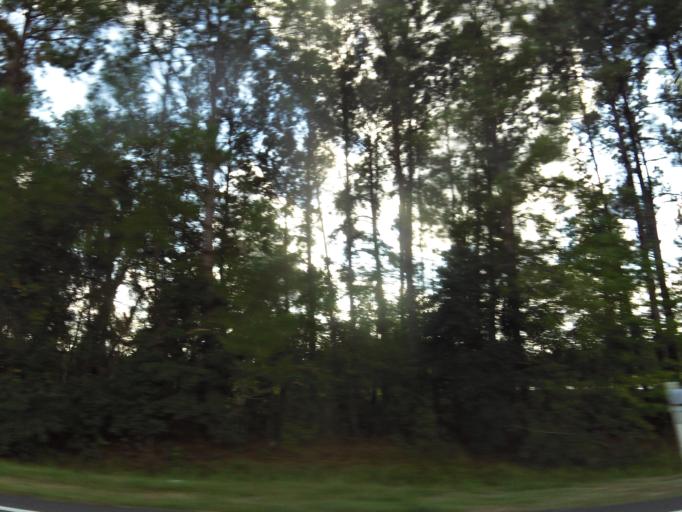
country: US
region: Georgia
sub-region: Lowndes County
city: Valdosta
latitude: 30.7809
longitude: -83.1591
